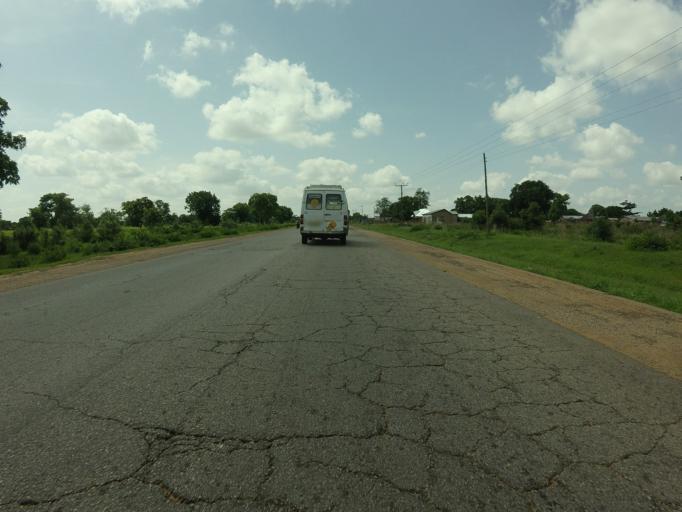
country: GH
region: Northern
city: Savelugu
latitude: 9.5759
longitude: -0.8343
